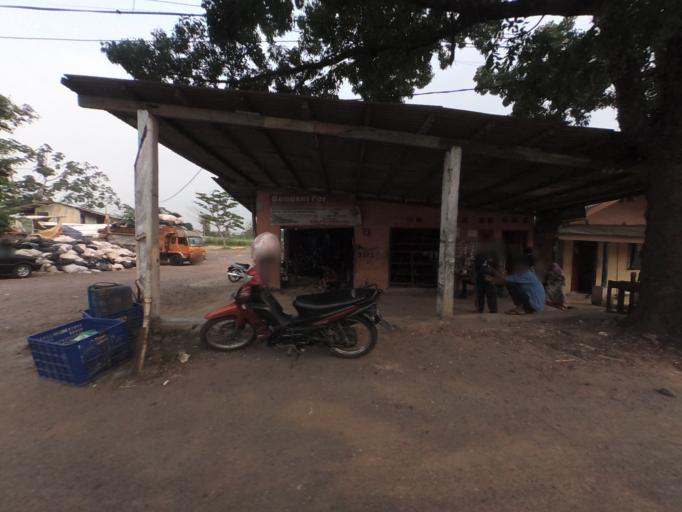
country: ID
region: West Java
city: Ciampea
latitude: -6.5692
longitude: 106.6688
